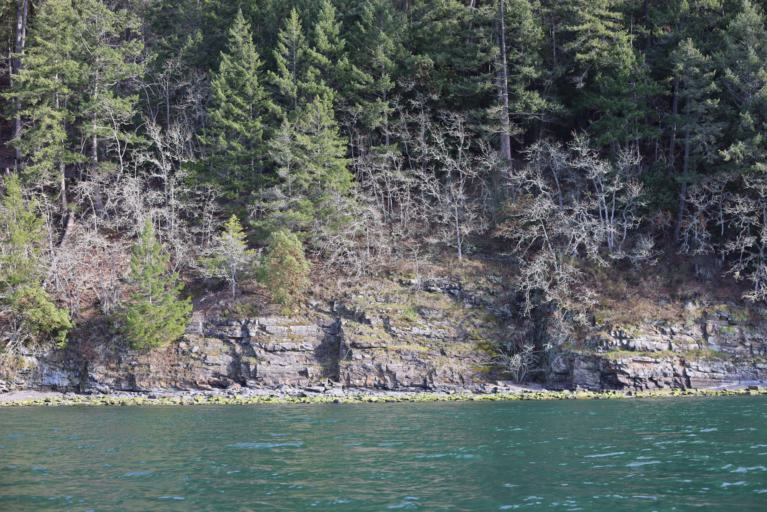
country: CA
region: British Columbia
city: Duncan
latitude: 48.7603
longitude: -123.6146
